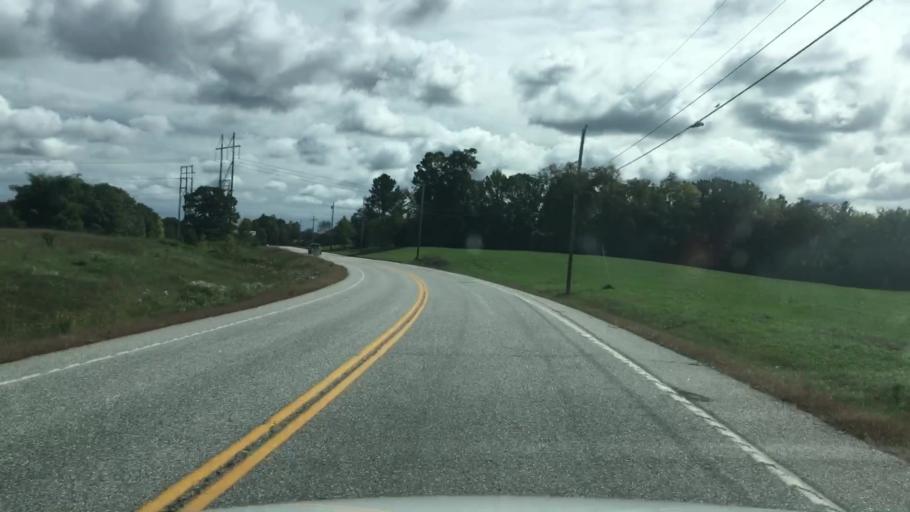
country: US
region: Maine
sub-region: Androscoggin County
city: Lisbon
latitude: 44.0235
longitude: -70.1797
